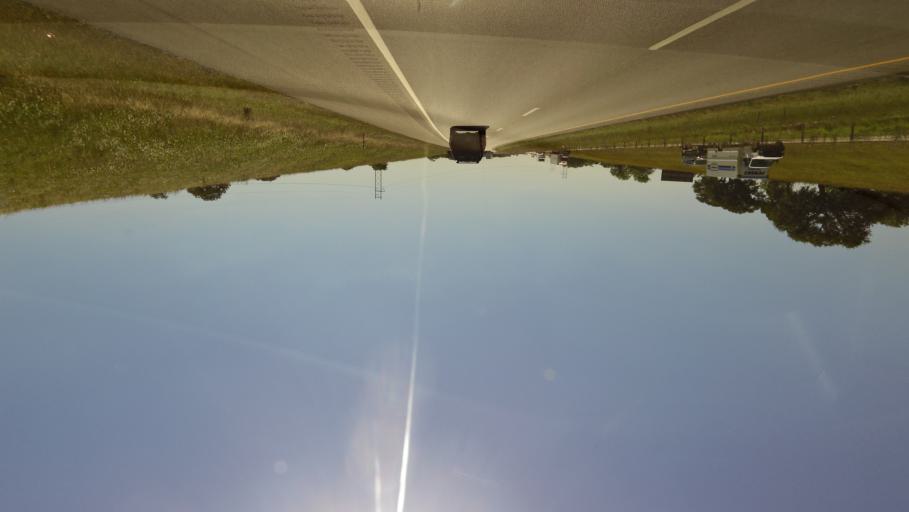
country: US
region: Texas
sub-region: Colorado County
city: Weimar
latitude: 29.6883
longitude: -96.7030
